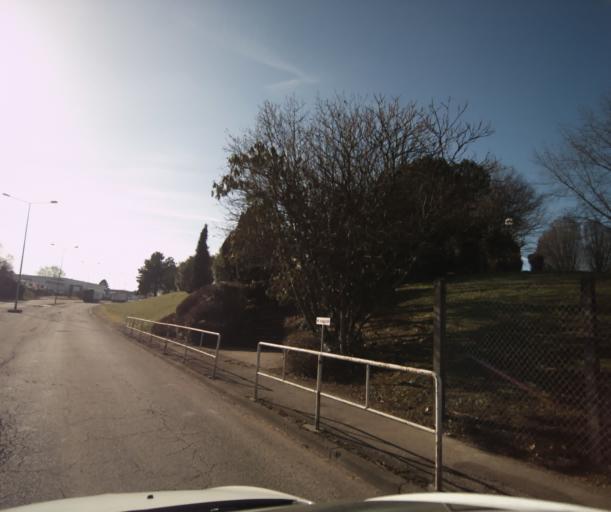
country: FR
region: Franche-Comte
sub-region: Departement du Doubs
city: Avanne-Aveney
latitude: 47.2286
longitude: 5.9770
